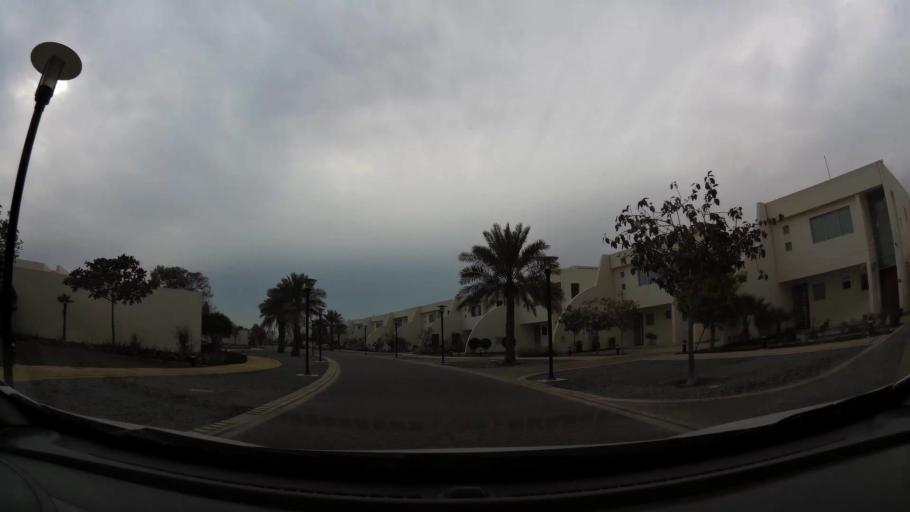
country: BH
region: Central Governorate
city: Dar Kulayb
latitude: 25.8398
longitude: 50.6170
